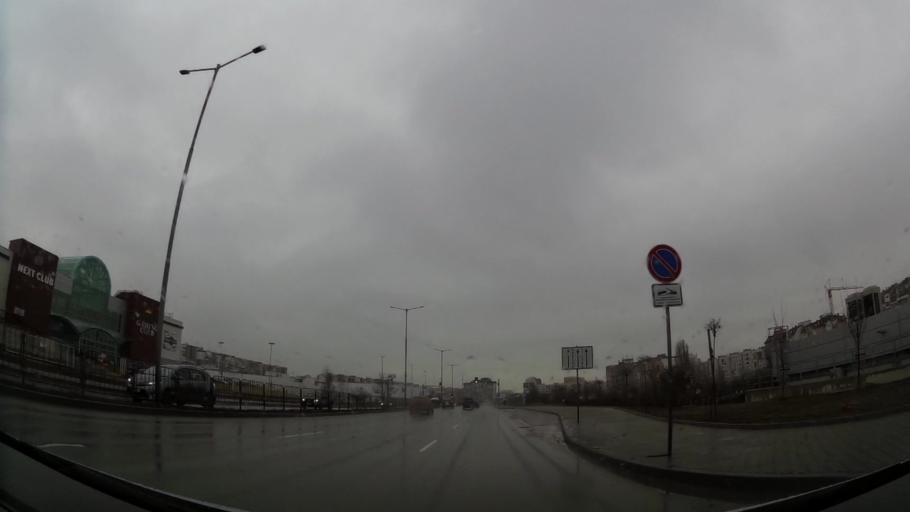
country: BG
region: Sofia-Capital
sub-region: Stolichna Obshtina
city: Sofia
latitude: 42.6361
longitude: 23.3732
